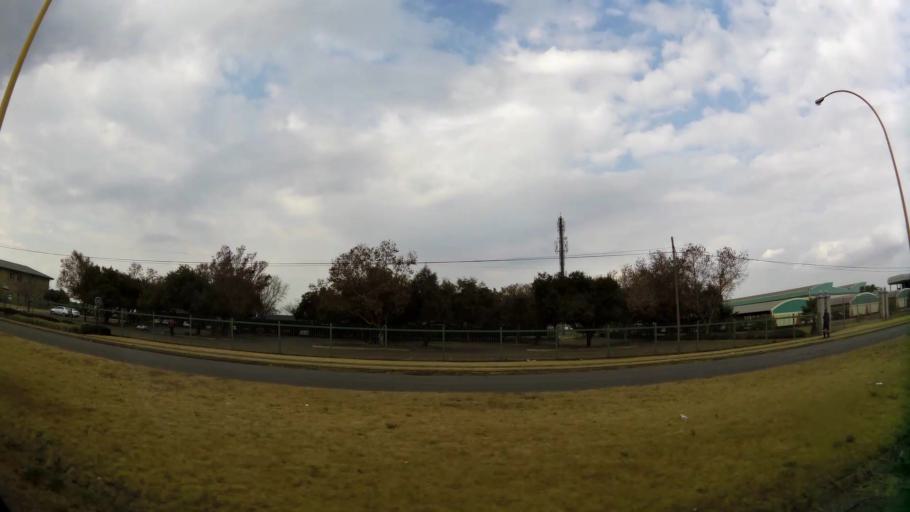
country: ZA
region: Gauteng
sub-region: Sedibeng District Municipality
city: Vanderbijlpark
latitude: -26.6769
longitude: 27.8182
